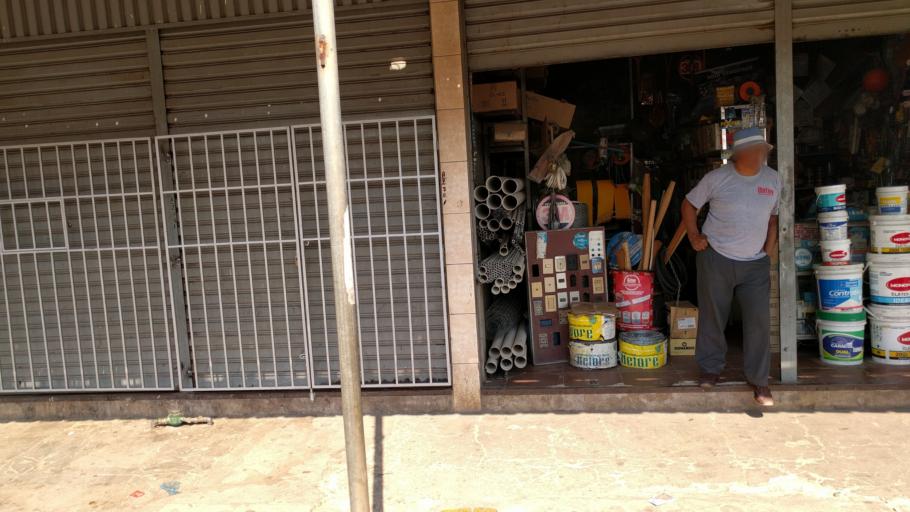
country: BO
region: Santa Cruz
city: Santa Cruz de la Sierra
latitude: -17.8254
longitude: -63.1670
